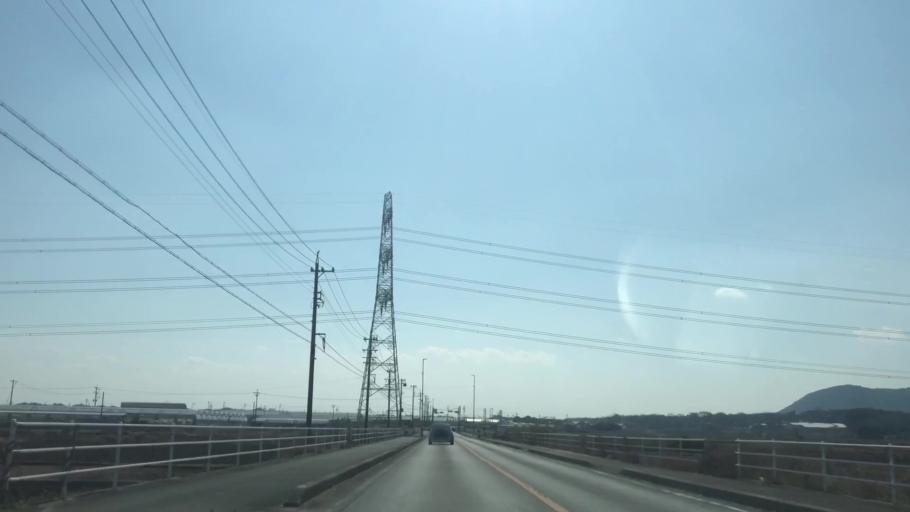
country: JP
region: Aichi
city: Tahara
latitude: 34.6416
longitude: 137.2390
